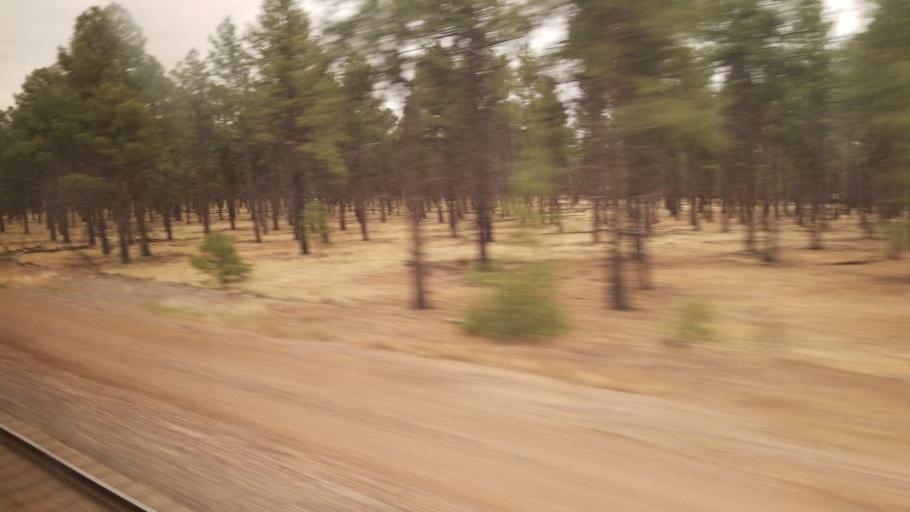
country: US
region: Arizona
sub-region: Coconino County
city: Parks
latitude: 35.2456
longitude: -112.0497
